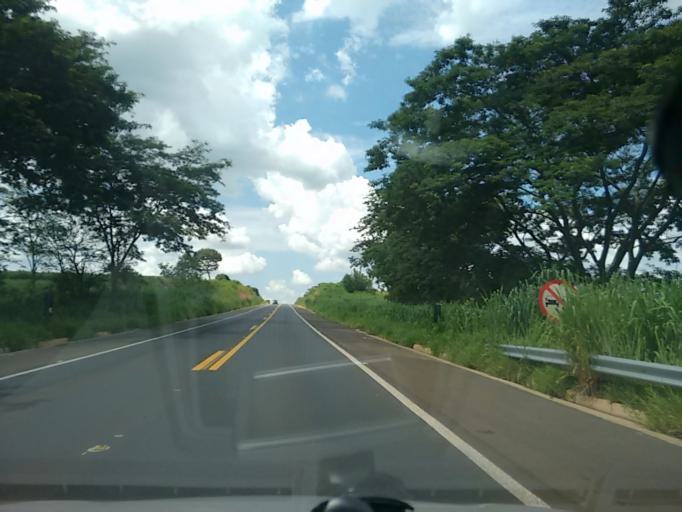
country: BR
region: Sao Paulo
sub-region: Osvaldo Cruz
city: Osvaldo Cruz
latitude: -21.8893
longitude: -50.8718
